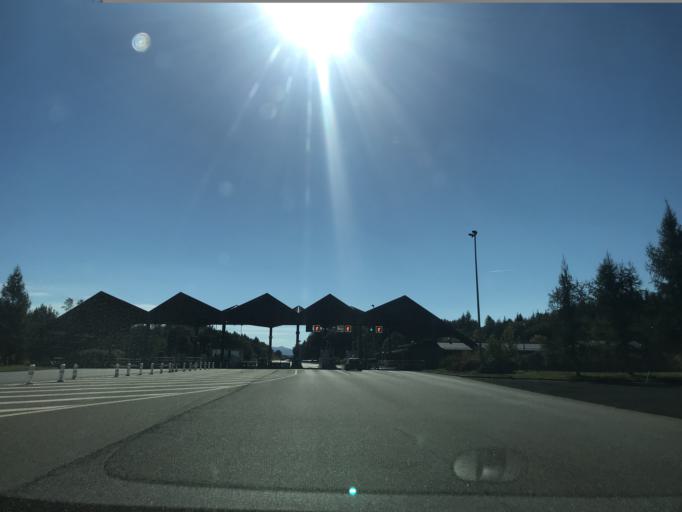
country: FR
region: Auvergne
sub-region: Departement du Puy-de-Dome
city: Saint-Sauves-d'Auvergne
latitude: 45.6672
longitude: 2.6818
